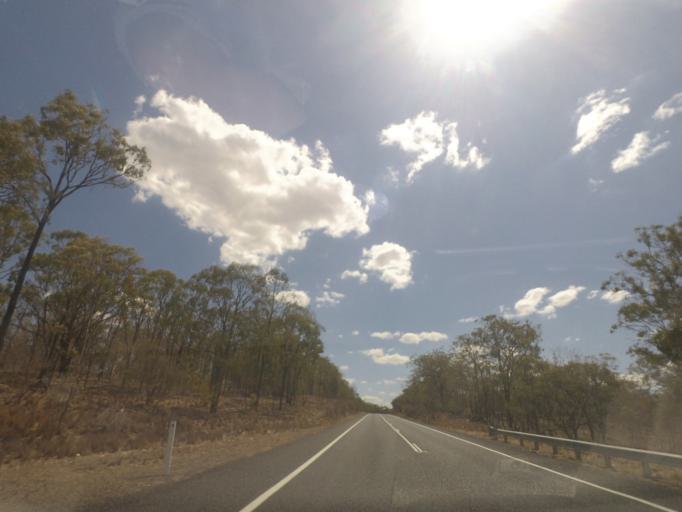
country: AU
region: Queensland
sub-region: Southern Downs
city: Warwick
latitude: -28.1617
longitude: 151.6853
